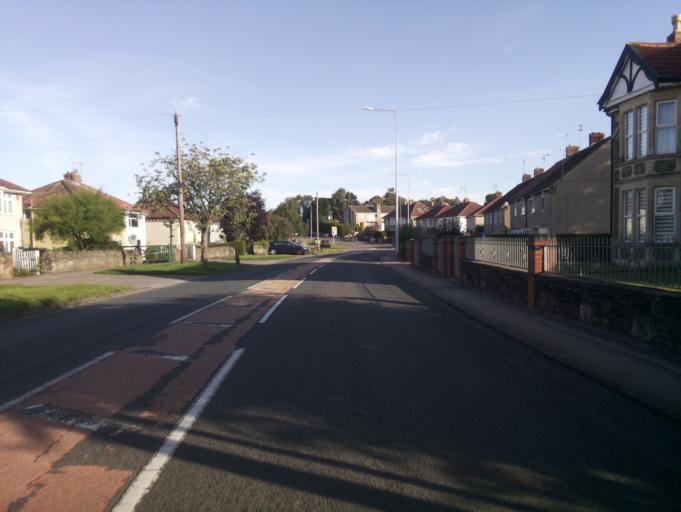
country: GB
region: England
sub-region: South Gloucestershire
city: Mangotsfield
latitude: 51.4872
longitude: -2.4922
